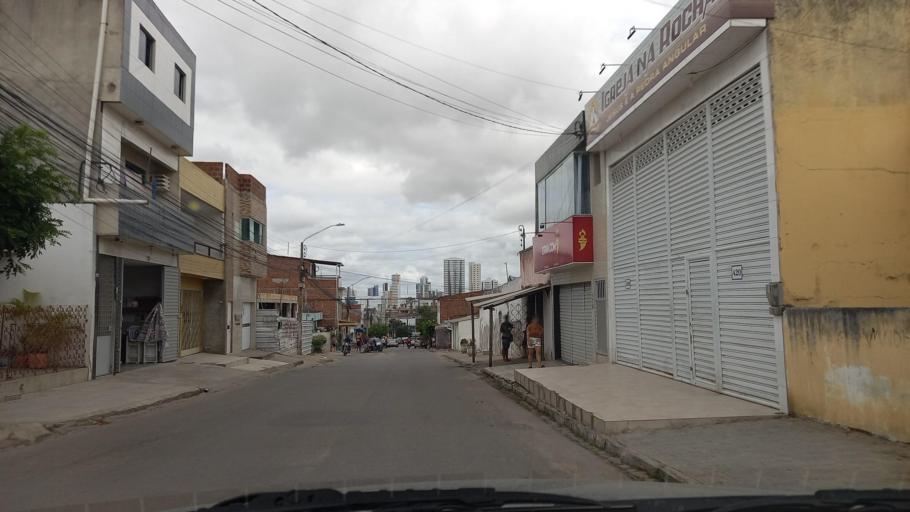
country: BR
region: Pernambuco
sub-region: Caruaru
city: Caruaru
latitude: -8.2720
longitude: -35.9577
